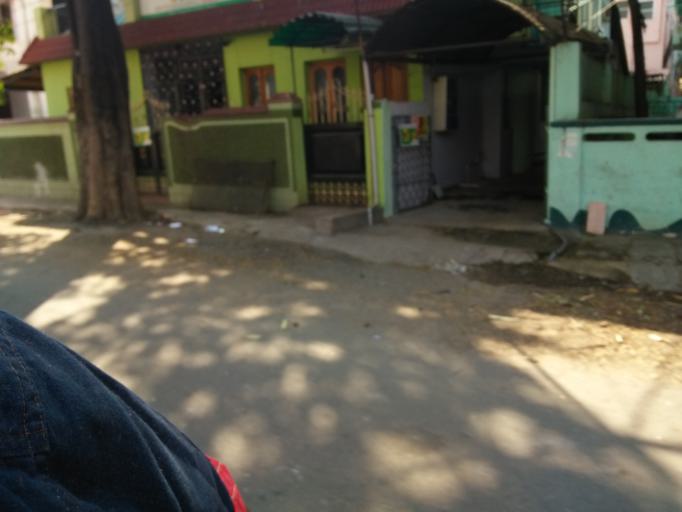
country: IN
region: Tamil Nadu
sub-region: Coimbatore
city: Coimbatore
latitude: 11.0203
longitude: 76.9641
